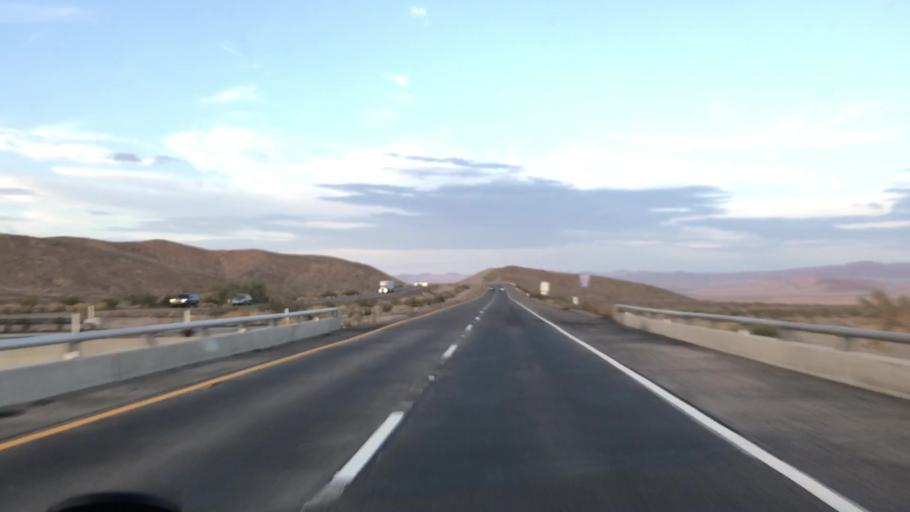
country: US
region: California
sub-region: San Bernardino County
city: Fort Irwin
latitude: 35.1963
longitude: -116.1340
